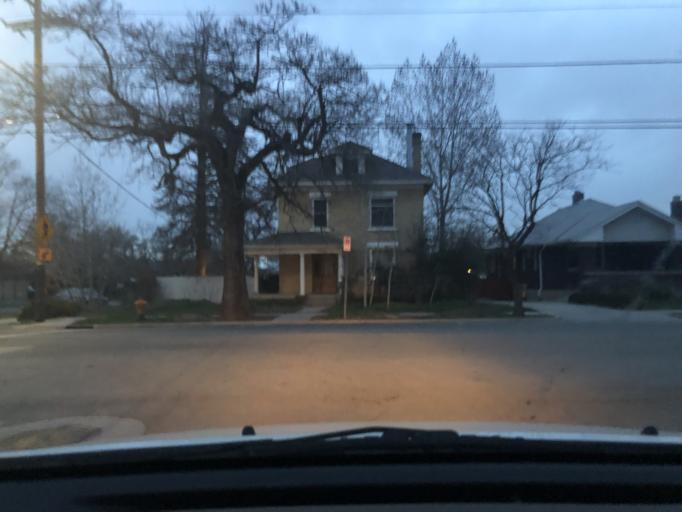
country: US
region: Utah
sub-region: Salt Lake County
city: South Salt Lake
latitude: 40.7392
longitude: -111.8653
